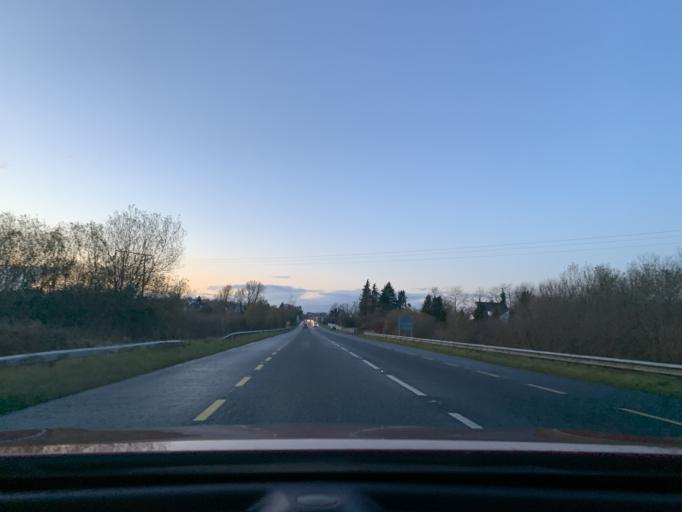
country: IE
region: Connaught
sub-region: County Leitrim
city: Carrick-on-Shannon
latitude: 53.9405
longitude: -8.0641
